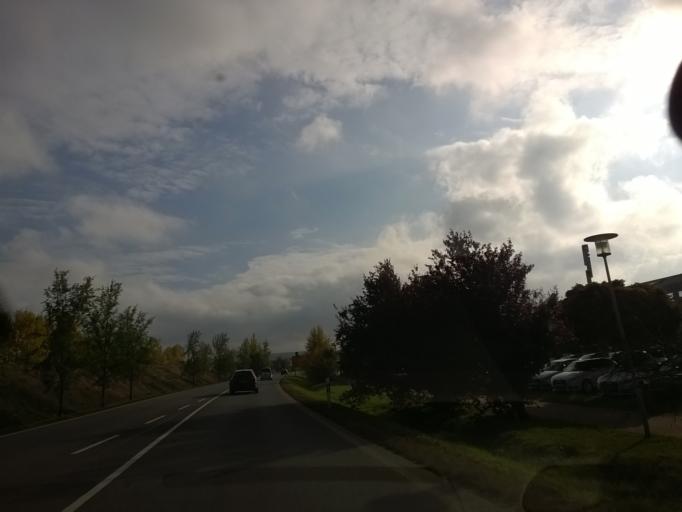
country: DE
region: Thuringia
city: Nordhausen
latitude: 51.4761
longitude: 10.8095
